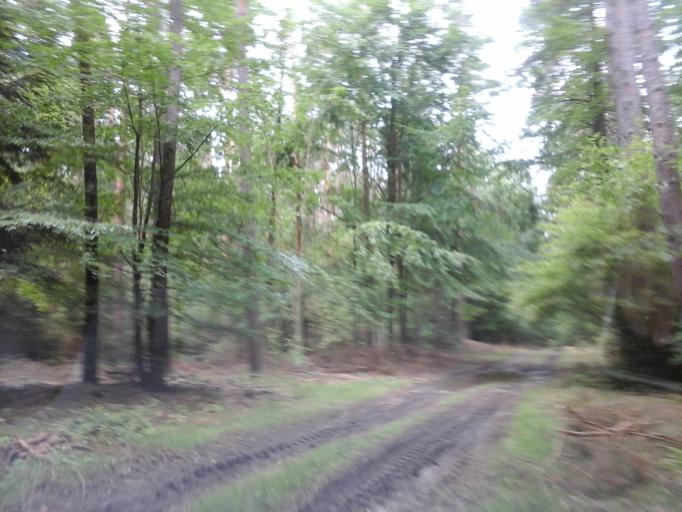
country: PL
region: West Pomeranian Voivodeship
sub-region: Powiat choszczenski
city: Pelczyce
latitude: 52.9560
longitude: 15.3495
